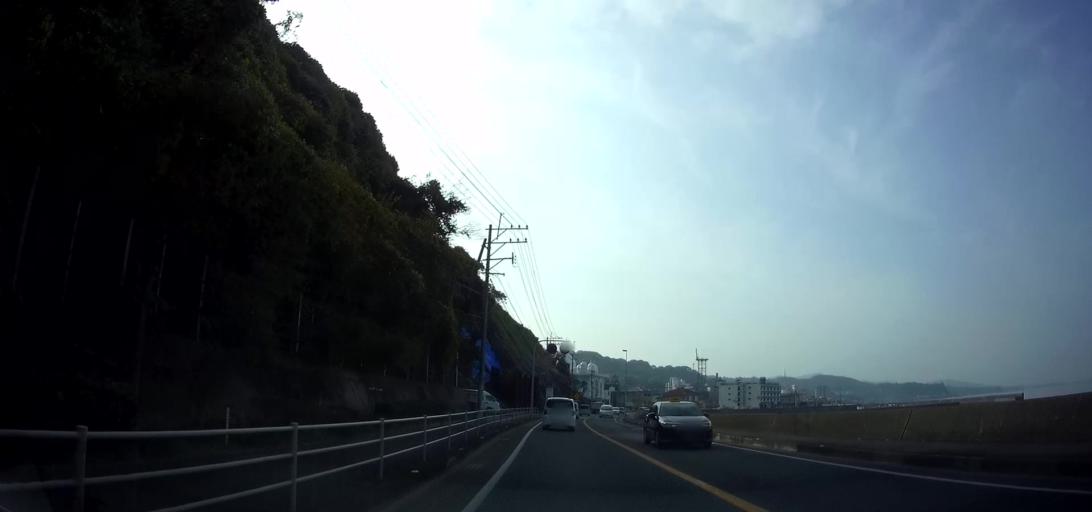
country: JP
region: Nagasaki
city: Shimabara
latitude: 32.7356
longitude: 130.2092
